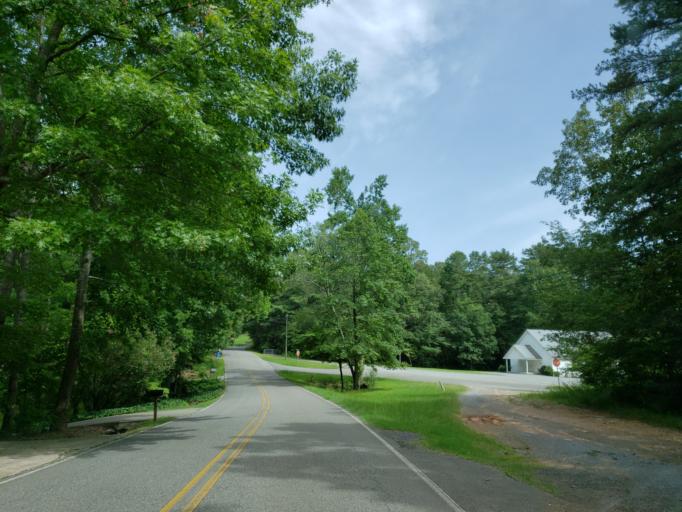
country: US
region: Georgia
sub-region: Pickens County
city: Nelson
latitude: 34.3701
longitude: -84.3820
